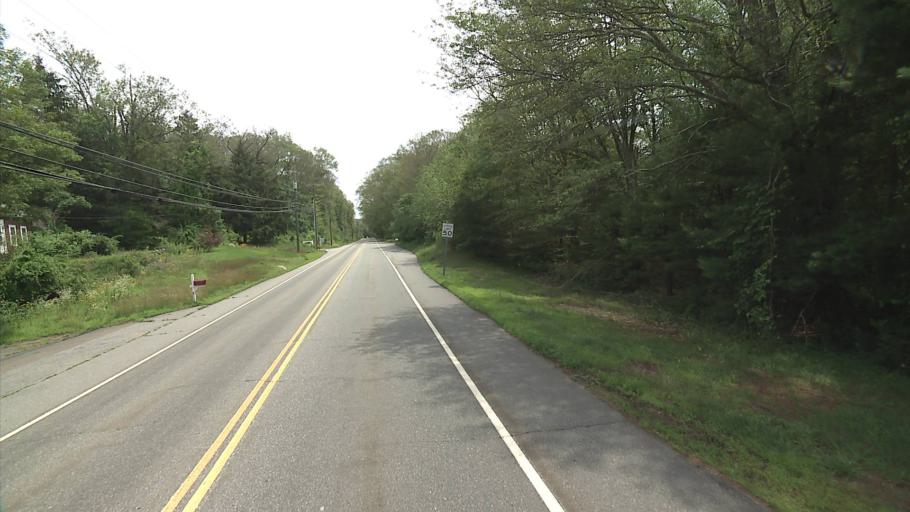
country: US
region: Connecticut
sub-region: New Haven County
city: Guilford
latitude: 41.3524
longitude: -72.6711
